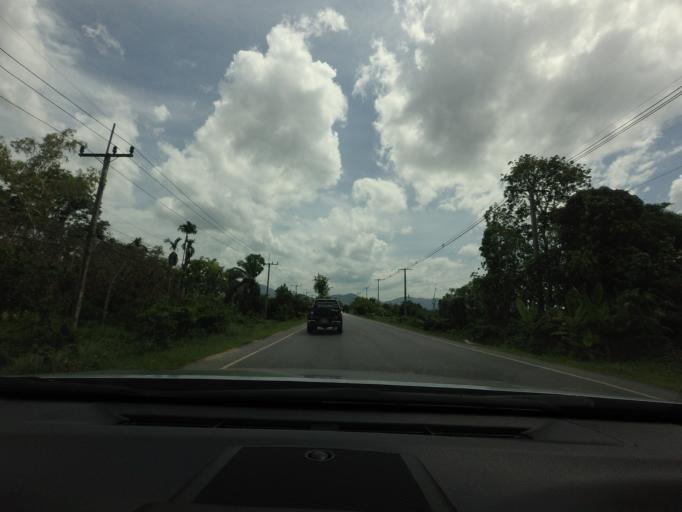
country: TH
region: Yala
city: Raman
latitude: 6.4628
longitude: 101.3758
